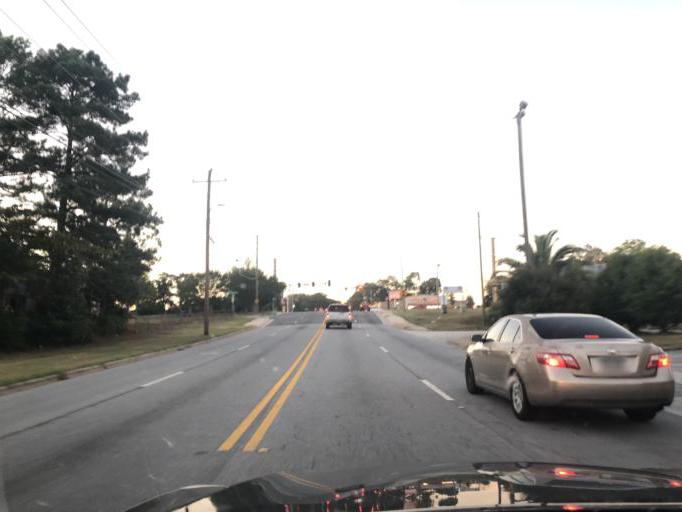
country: US
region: Georgia
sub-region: Muscogee County
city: Columbus
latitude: 32.4790
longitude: -84.8987
